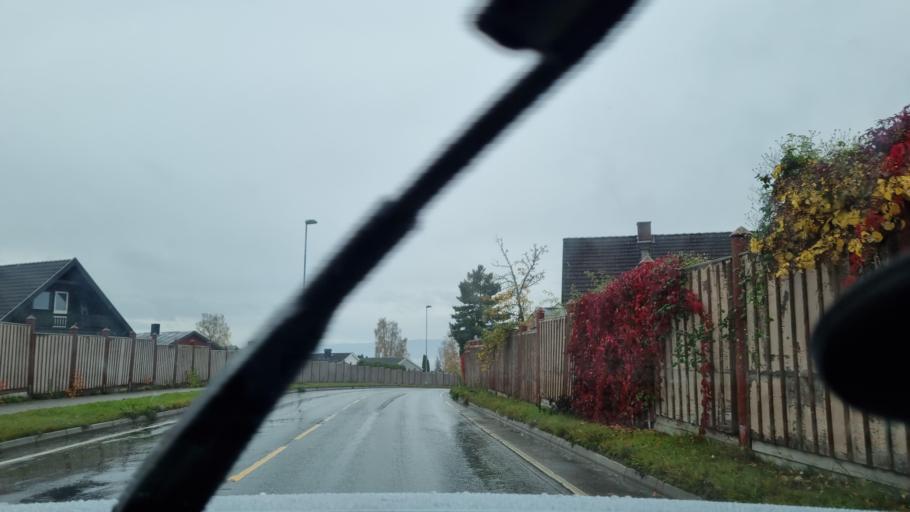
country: NO
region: Hedmark
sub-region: Hamar
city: Hamar
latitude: 60.8124
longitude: 11.0607
